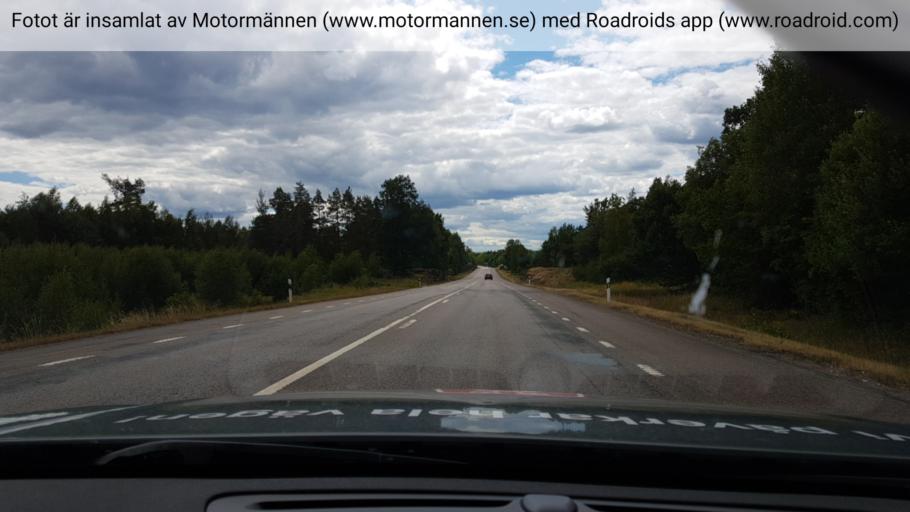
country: SE
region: Kalmar
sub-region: Vasterviks Kommun
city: Ankarsrum
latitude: 57.5837
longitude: 16.4857
